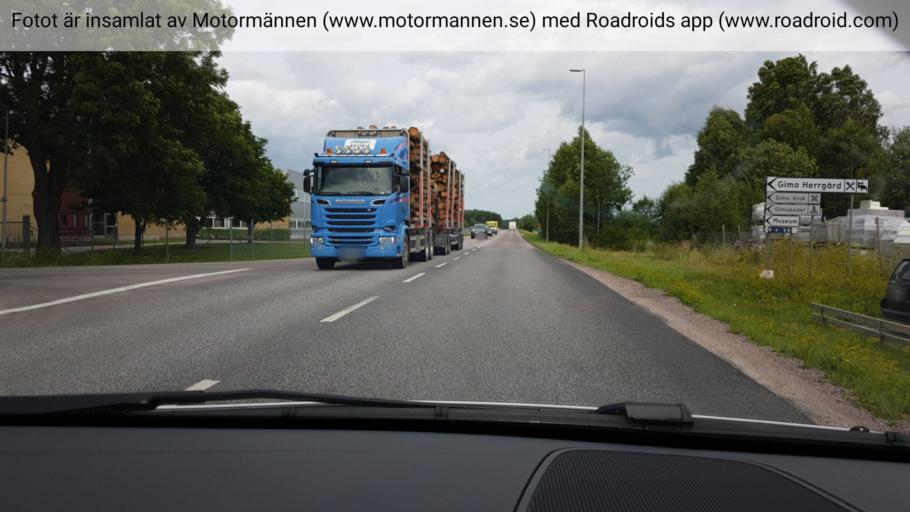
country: SE
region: Uppsala
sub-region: Osthammars Kommun
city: Gimo
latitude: 60.1784
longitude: 18.1906
